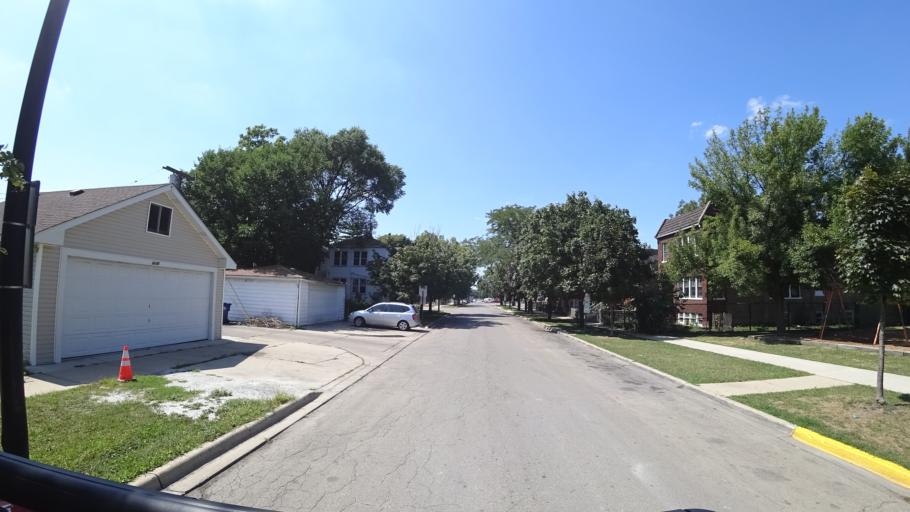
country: US
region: Illinois
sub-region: Cook County
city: Cicero
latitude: 41.8531
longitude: -87.7423
